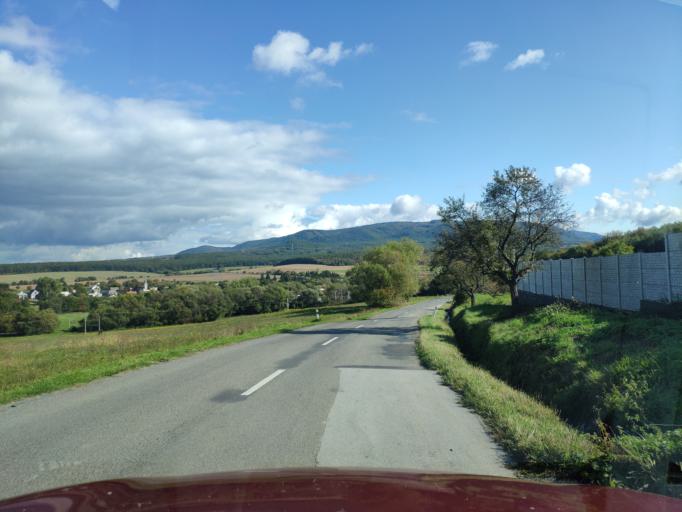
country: SK
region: Presovsky
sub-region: Okres Presov
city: Presov
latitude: 48.9497
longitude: 21.2948
